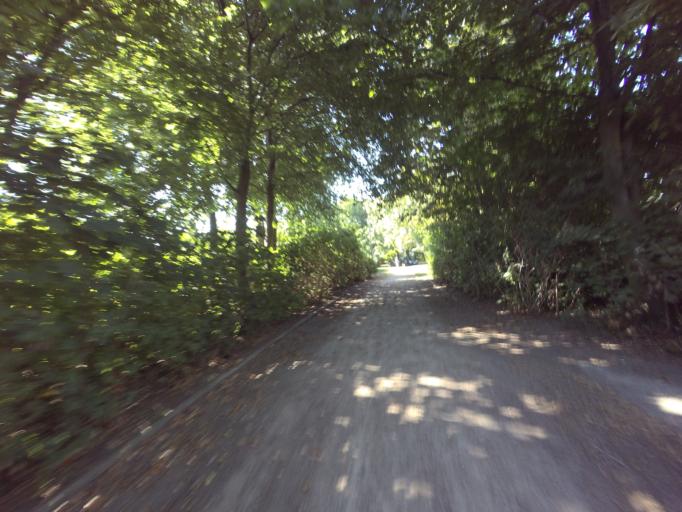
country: SE
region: Skane
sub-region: Trelleborgs Kommun
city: Skare
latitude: 55.4034
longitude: 13.0831
